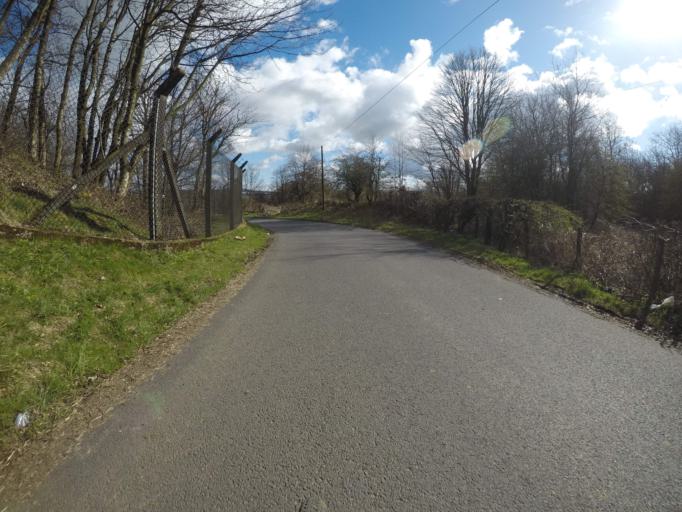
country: GB
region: Scotland
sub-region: North Ayrshire
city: Beith
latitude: 55.7291
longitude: -4.6062
